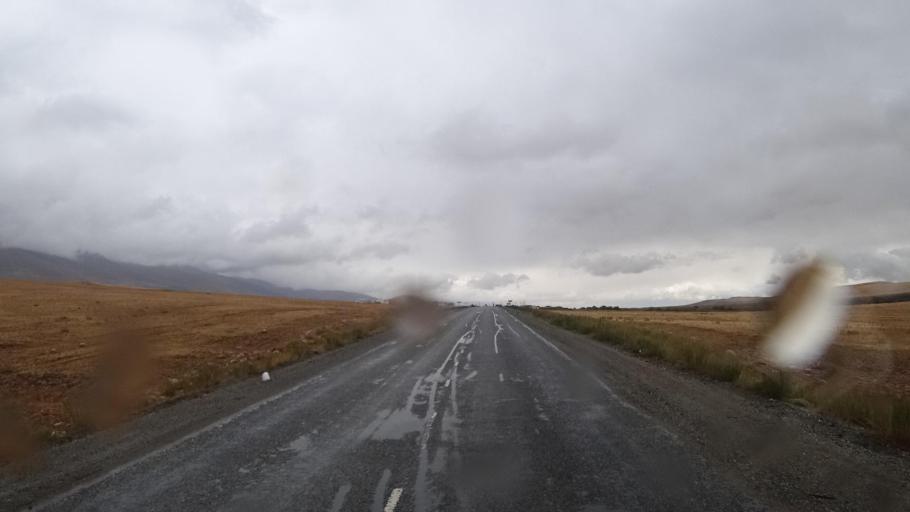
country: KG
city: Sosnovka
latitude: 42.2164
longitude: 73.6853
